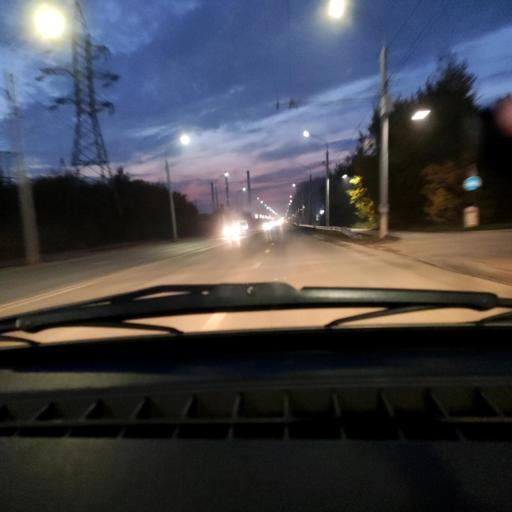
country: RU
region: Bashkortostan
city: Ufa
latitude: 54.7910
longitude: 56.0913
